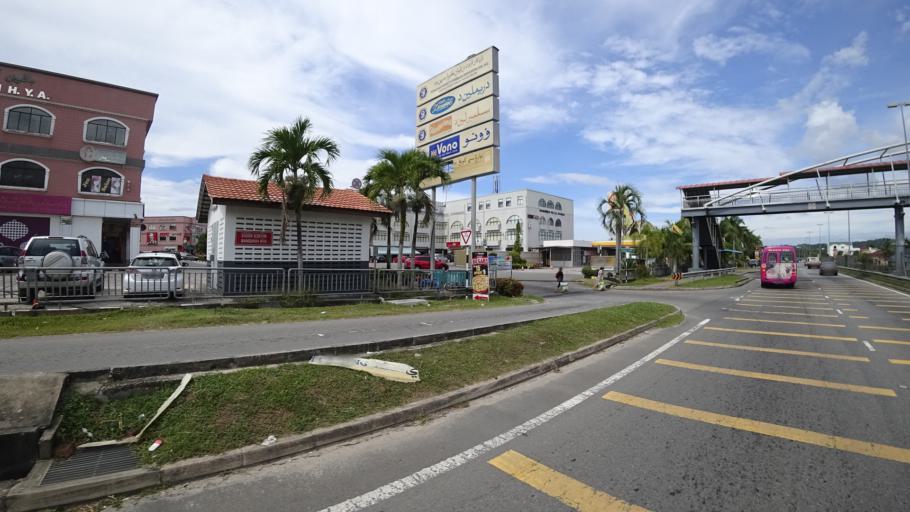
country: BN
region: Brunei and Muara
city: Bandar Seri Begawan
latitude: 4.8869
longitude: 114.8408
